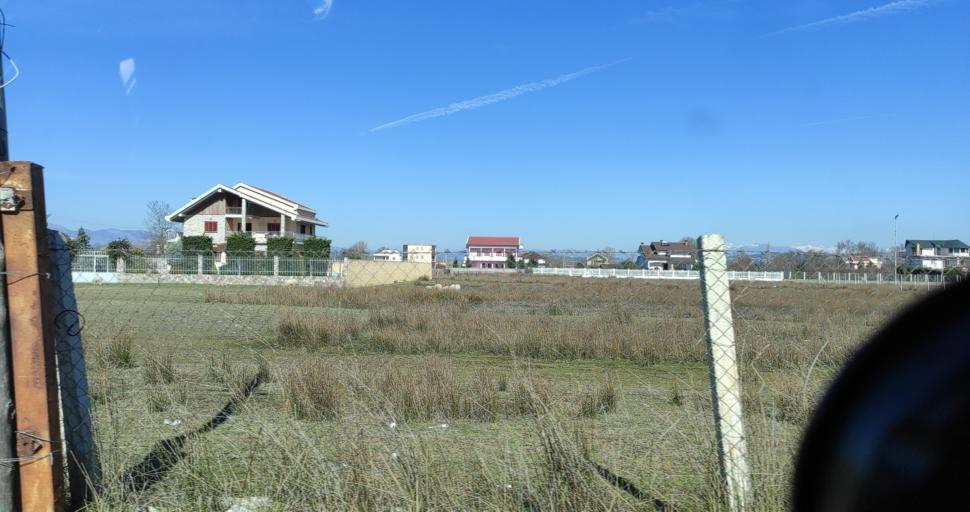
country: AL
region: Shkoder
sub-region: Rrethi i Shkodres
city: Velipoje
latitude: 41.8671
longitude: 19.4145
